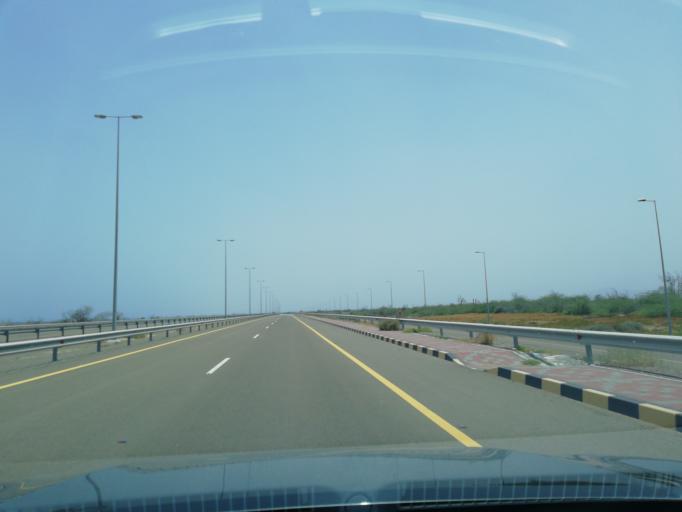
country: OM
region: Al Batinah
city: Shinas
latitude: 24.8845
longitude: 56.4028
